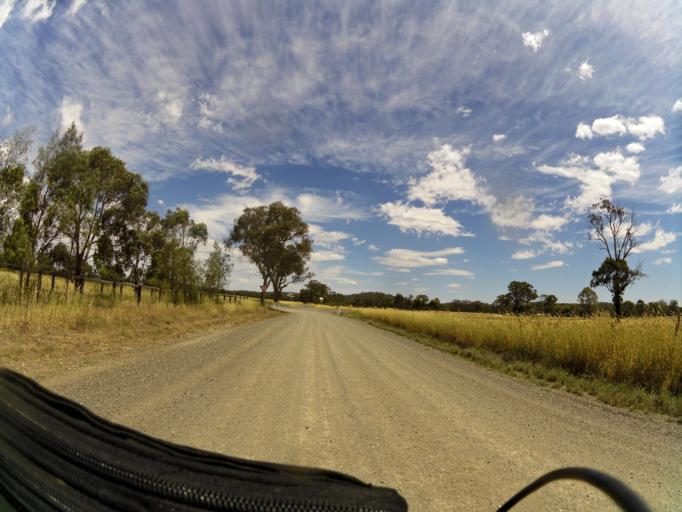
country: AU
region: Victoria
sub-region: Campaspe
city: Kyabram
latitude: -36.7582
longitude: 145.1021
